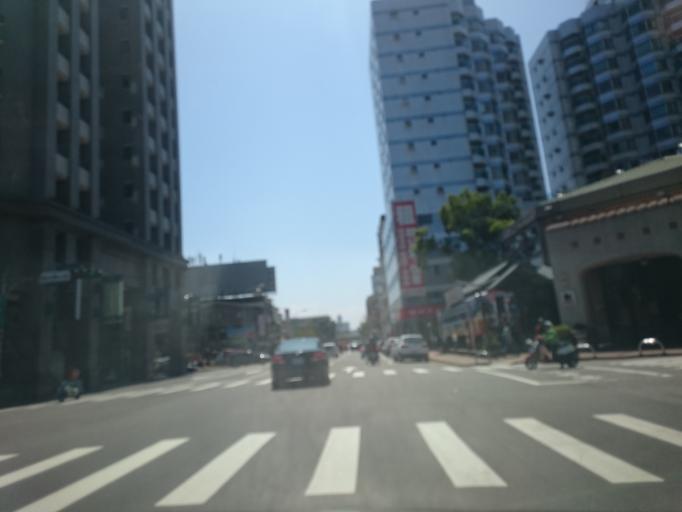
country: TW
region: Taiwan
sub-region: Taichung City
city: Taichung
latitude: 24.1564
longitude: 120.6902
